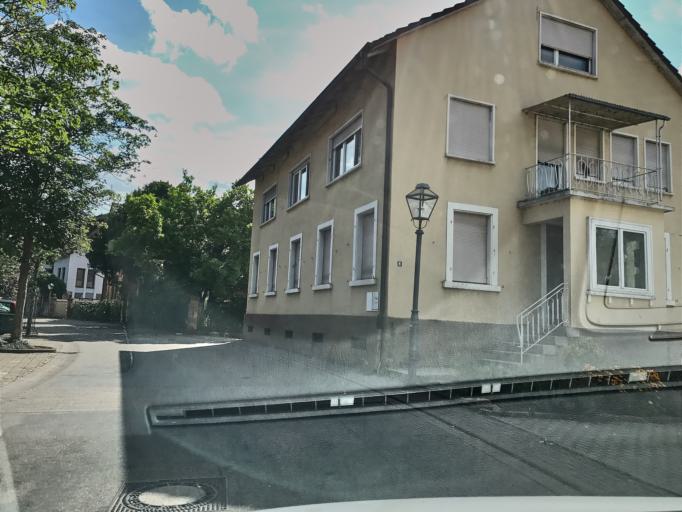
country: DE
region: Baden-Wuerttemberg
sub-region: Freiburg Region
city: Biberach
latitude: 48.3458
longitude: 8.0629
